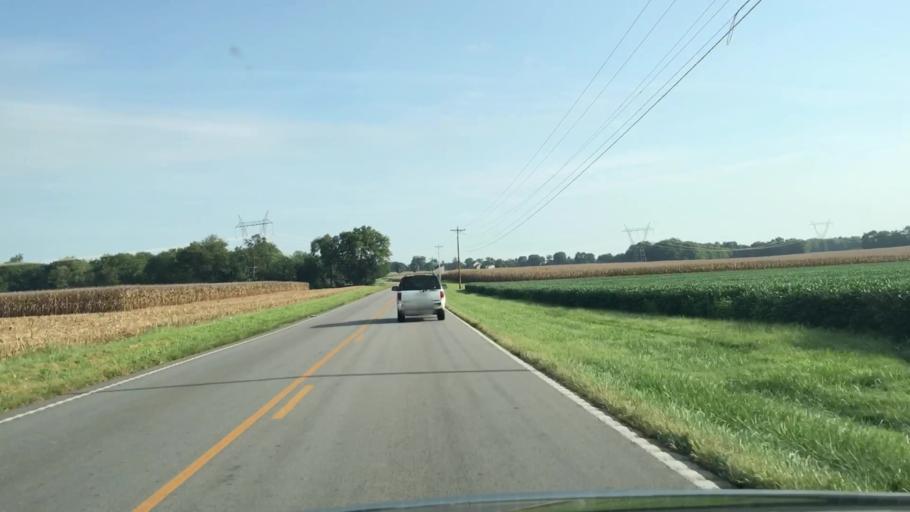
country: US
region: Kentucky
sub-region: Todd County
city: Guthrie
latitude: 36.6642
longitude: -87.1984
